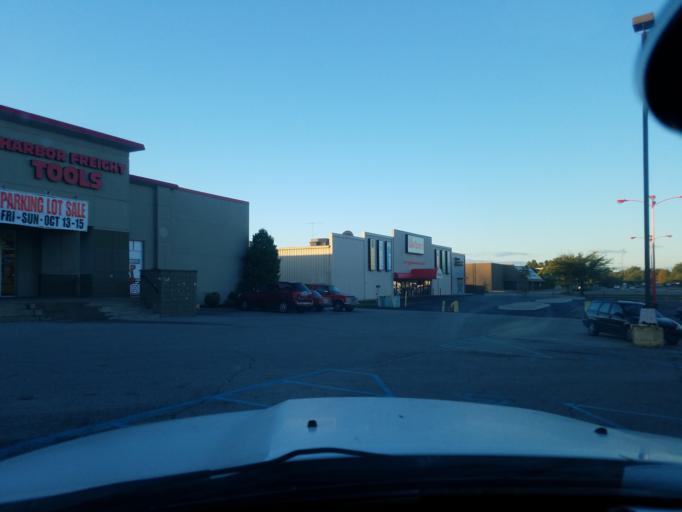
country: US
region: Indiana
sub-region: Clark County
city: Clarksville
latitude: 38.3117
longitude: -85.7630
